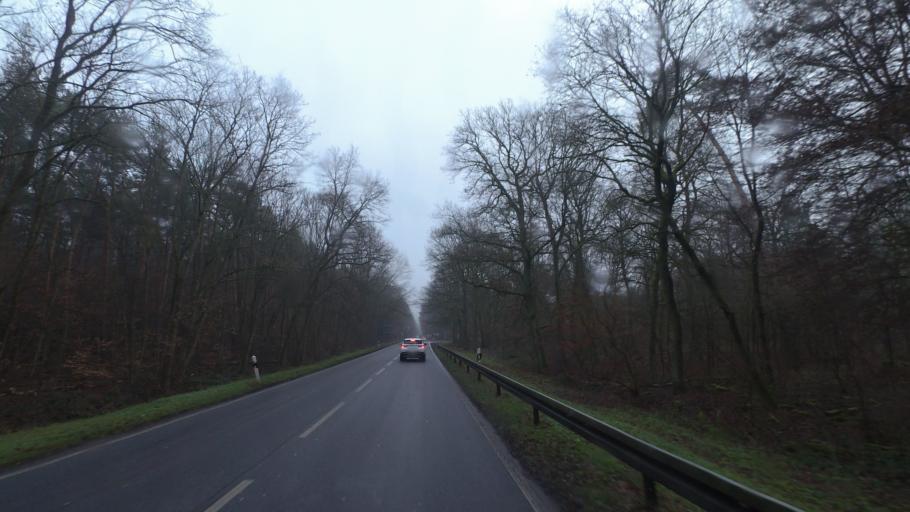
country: DE
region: Hesse
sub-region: Regierungsbezirk Darmstadt
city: Rodgau
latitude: 50.0611
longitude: 8.8967
